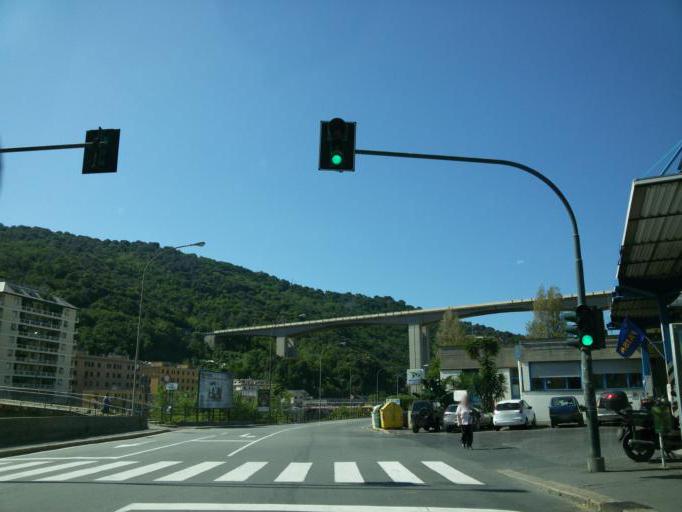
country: IT
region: Liguria
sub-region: Provincia di Genova
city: Piccarello
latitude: 44.4363
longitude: 8.9620
